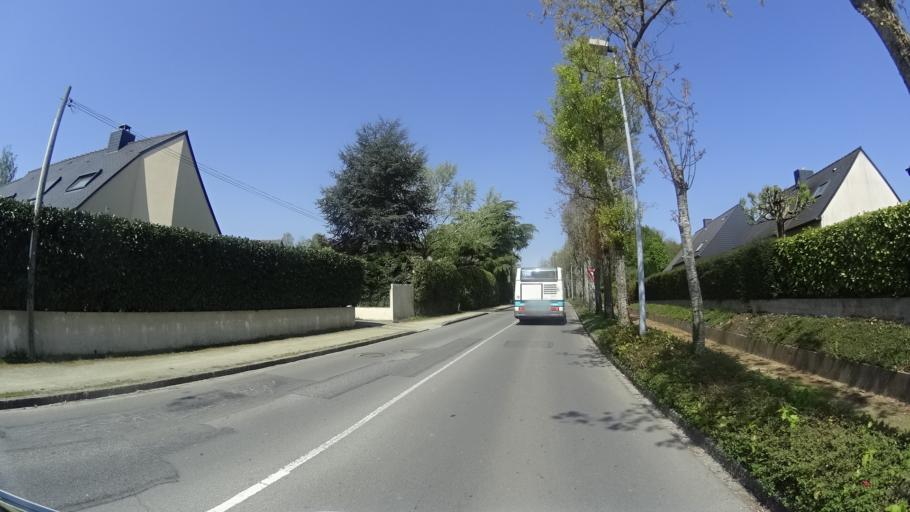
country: FR
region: Brittany
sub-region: Departement d'Ille-et-Vilaine
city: Chavagne
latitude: 48.0580
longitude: -1.7880
